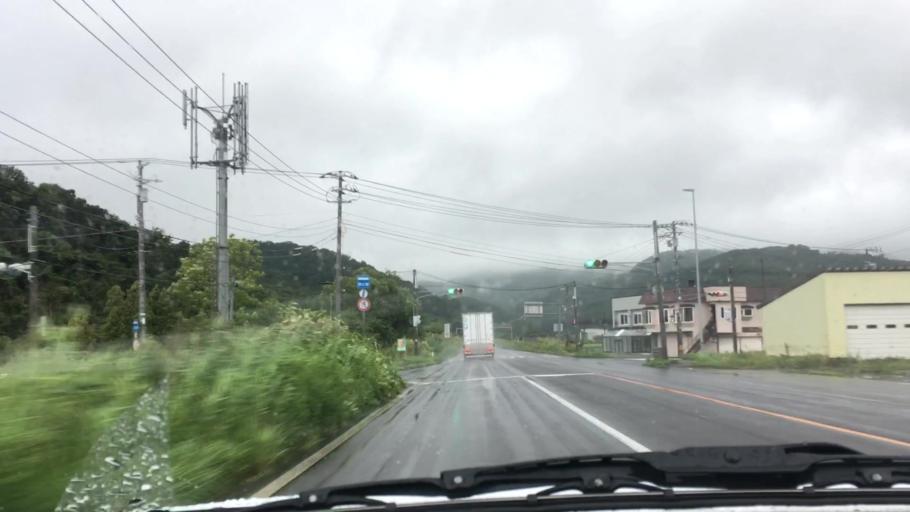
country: JP
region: Hokkaido
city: Niseko Town
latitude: 42.5990
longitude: 140.6357
